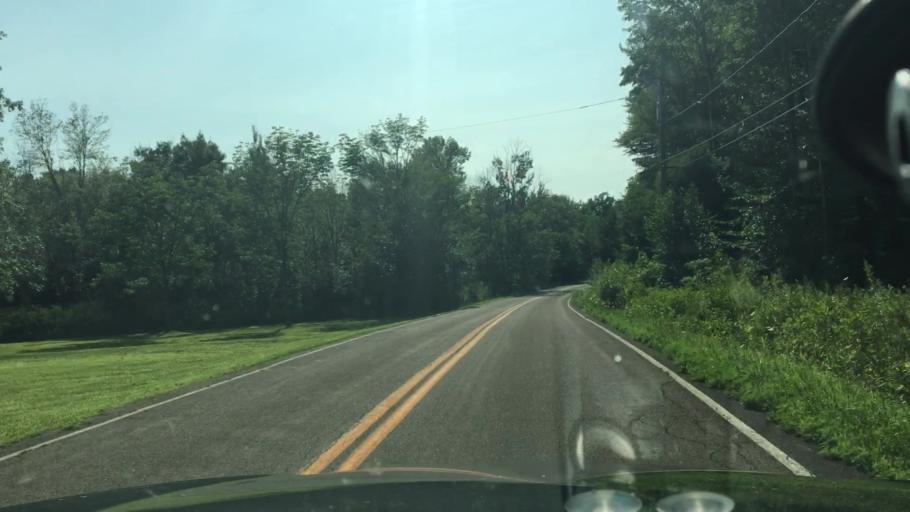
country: US
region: New York
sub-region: Erie County
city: North Collins
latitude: 42.6196
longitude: -78.9457
